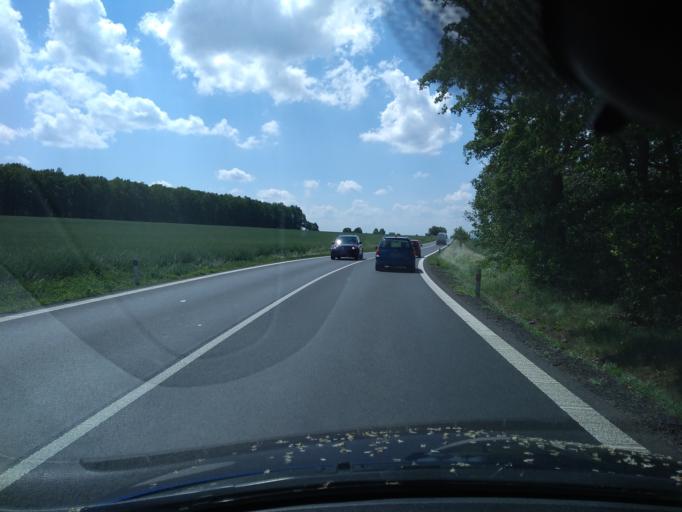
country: CZ
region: Plzensky
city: Chlumcany
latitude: 49.6389
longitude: 13.3350
